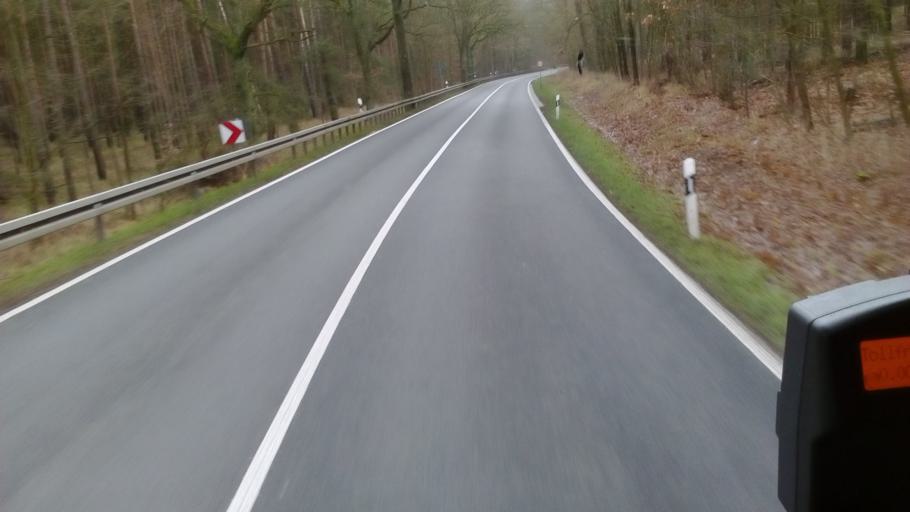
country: DE
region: Brandenburg
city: Heiligengrabe
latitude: 53.1402
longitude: 12.2845
